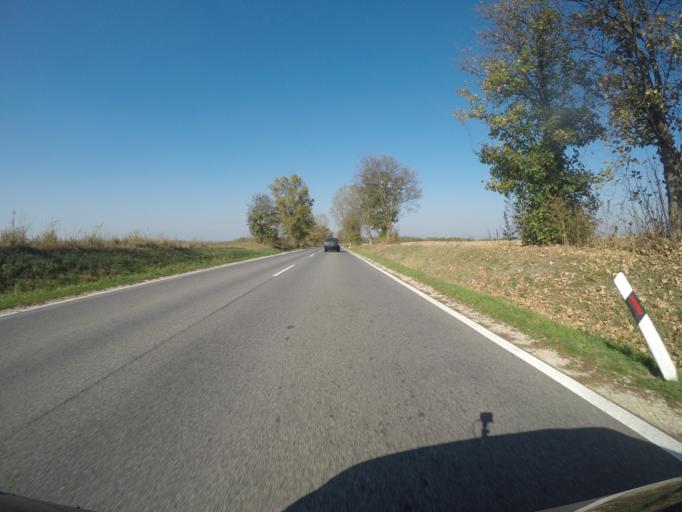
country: HU
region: Tolna
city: Tengelic
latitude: 46.5525
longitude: 18.6514
